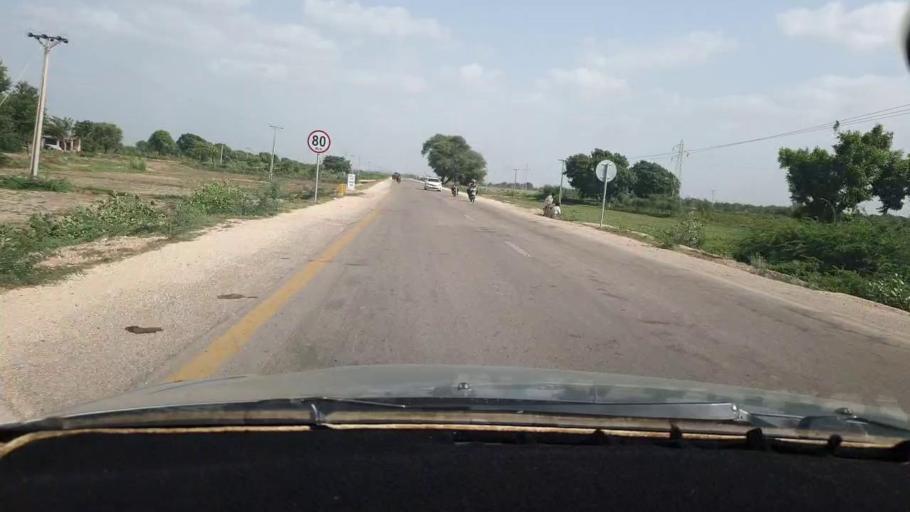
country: PK
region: Sindh
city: Naukot
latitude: 24.8754
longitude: 69.3676
